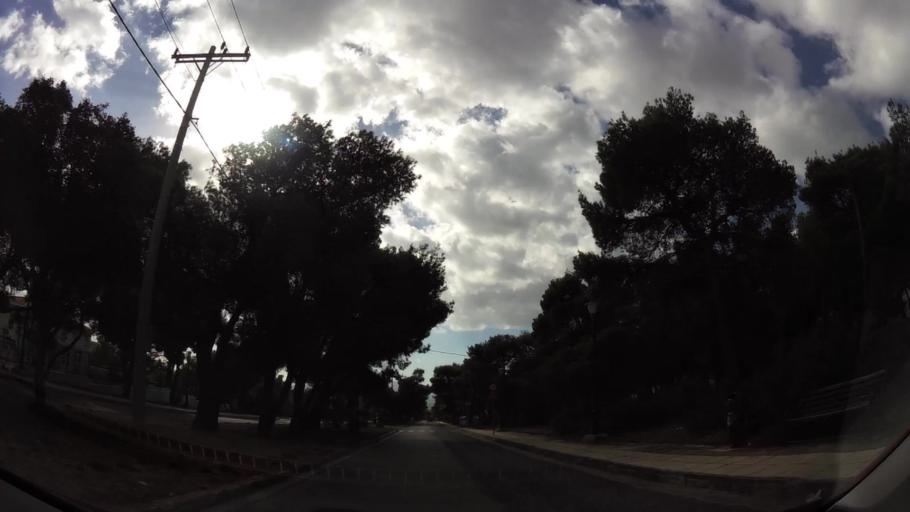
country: GR
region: Attica
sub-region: Nomarchia Anatolikis Attikis
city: Thrakomakedones
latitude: 38.1342
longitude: 23.7567
